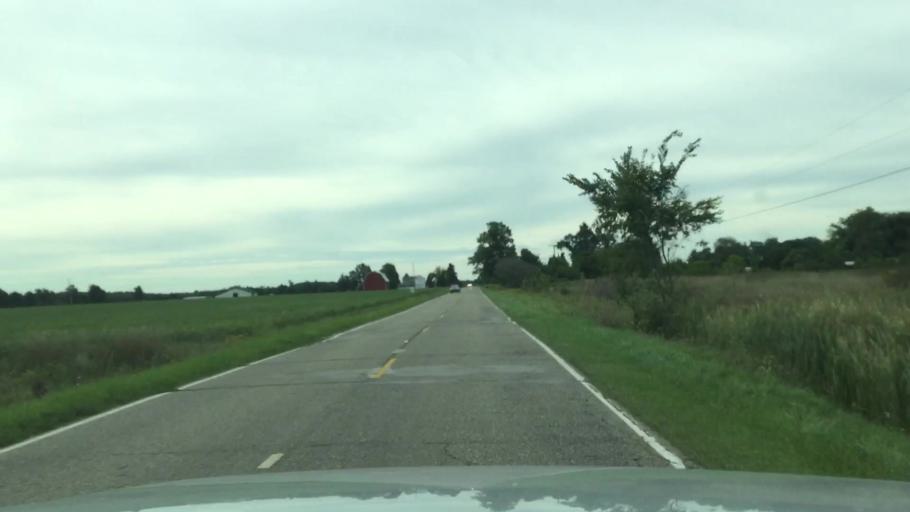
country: US
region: Michigan
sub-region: Genesee County
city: Montrose
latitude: 43.0833
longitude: -83.9877
